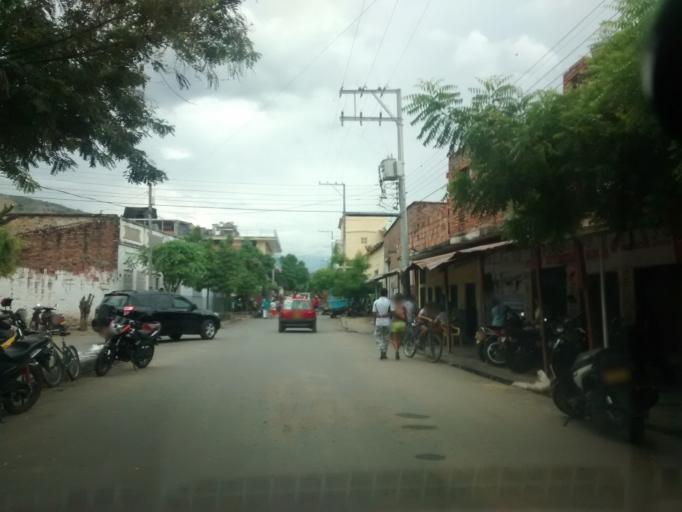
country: CO
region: Cundinamarca
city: Tocaima
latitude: 4.4593
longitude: -74.6353
